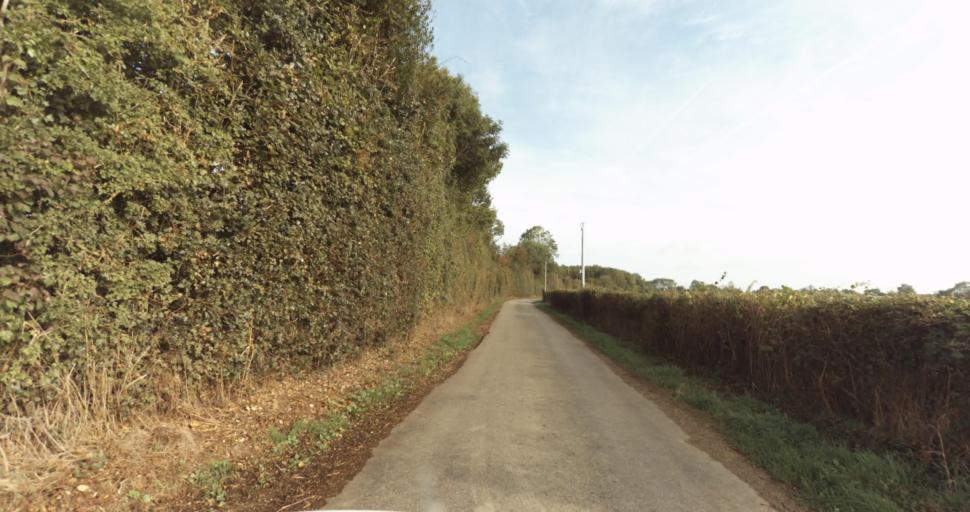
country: FR
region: Lower Normandy
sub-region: Departement de l'Orne
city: Vimoutiers
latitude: 48.9067
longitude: 0.2976
